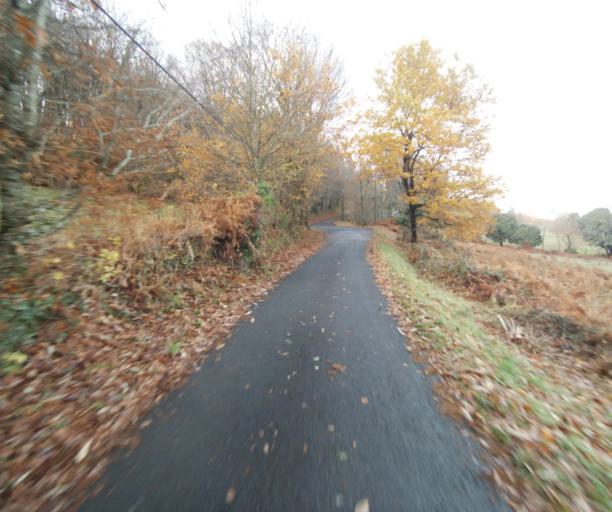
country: FR
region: Limousin
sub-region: Departement de la Correze
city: Cornil
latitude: 45.1969
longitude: 1.6945
